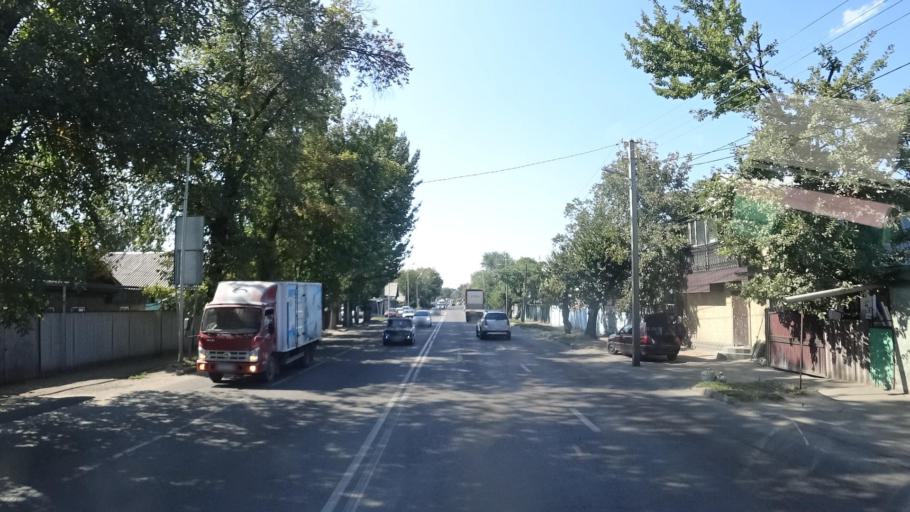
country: KZ
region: Almaty Oblysy
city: Pervomayskiy
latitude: 43.3535
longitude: 76.9527
